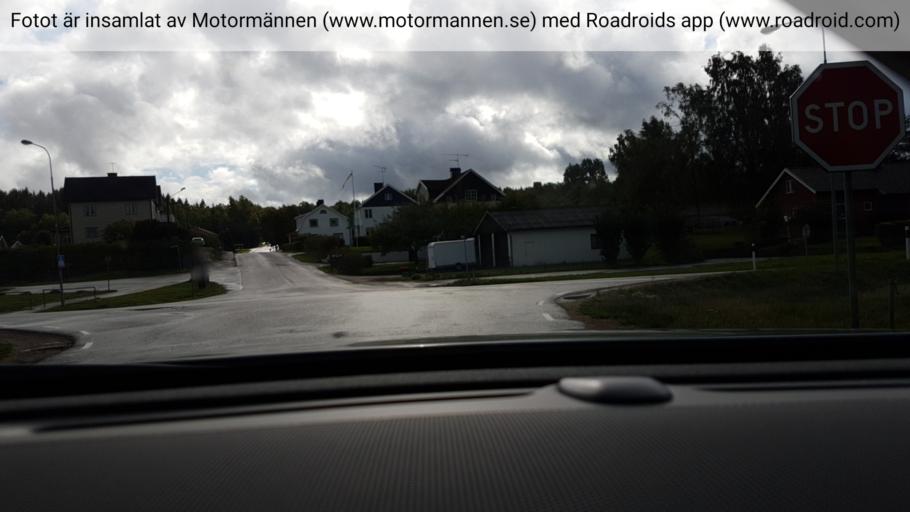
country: SE
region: Vaestra Goetaland
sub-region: Svenljunga Kommun
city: Svenljunga
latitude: 57.4145
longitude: 12.9716
